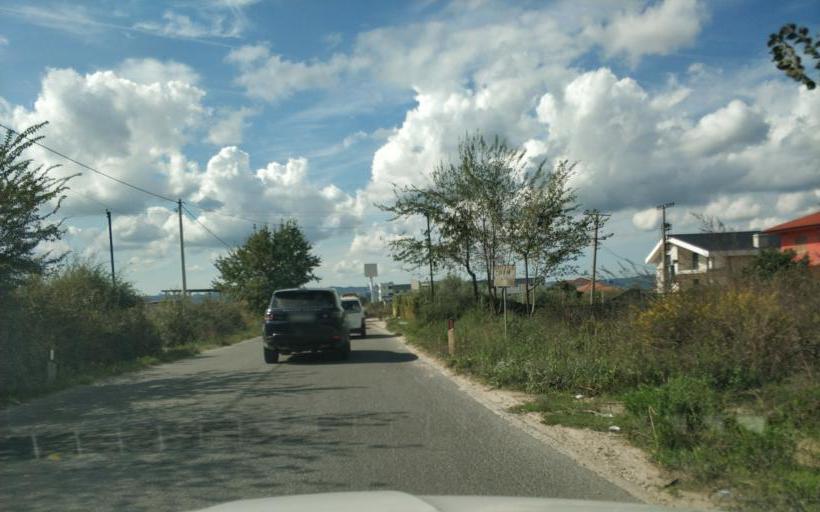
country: AL
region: Durres
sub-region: Rrethi i Krujes
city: Nikel
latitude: 41.4792
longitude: 19.7572
